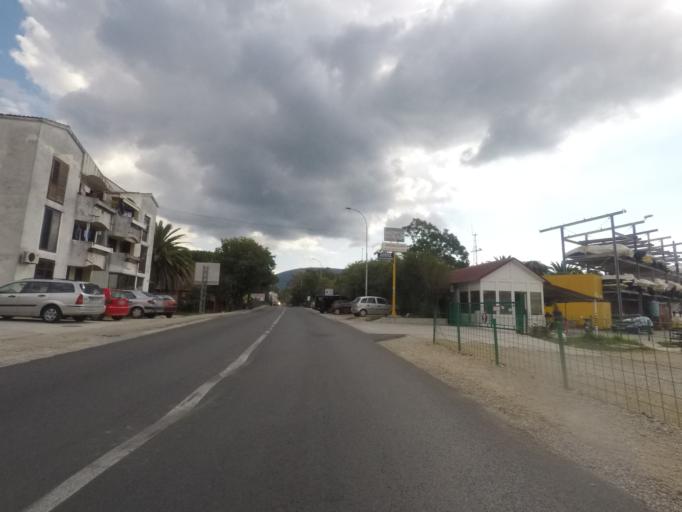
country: ME
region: Herceg Novi
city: Herceg-Novi
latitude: 42.4494
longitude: 18.5739
